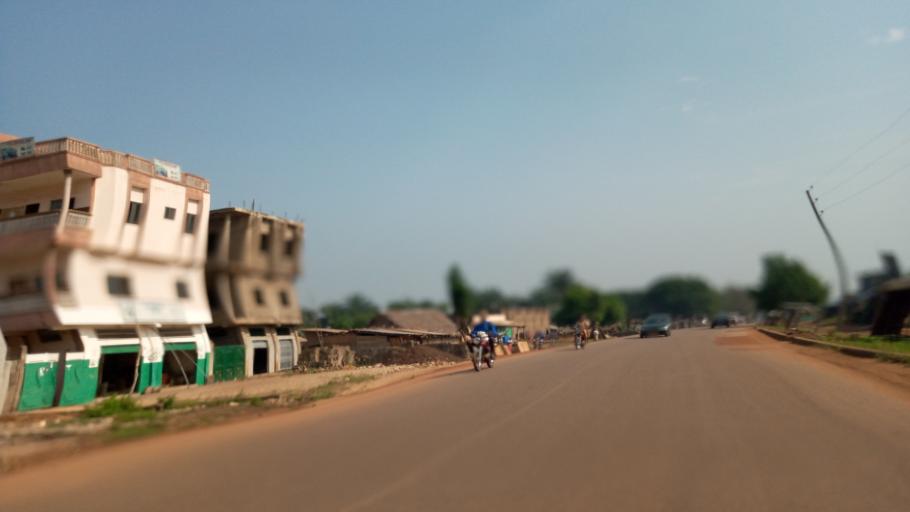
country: BJ
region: Queme
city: Porto-Novo
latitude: 6.5383
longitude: 2.6491
